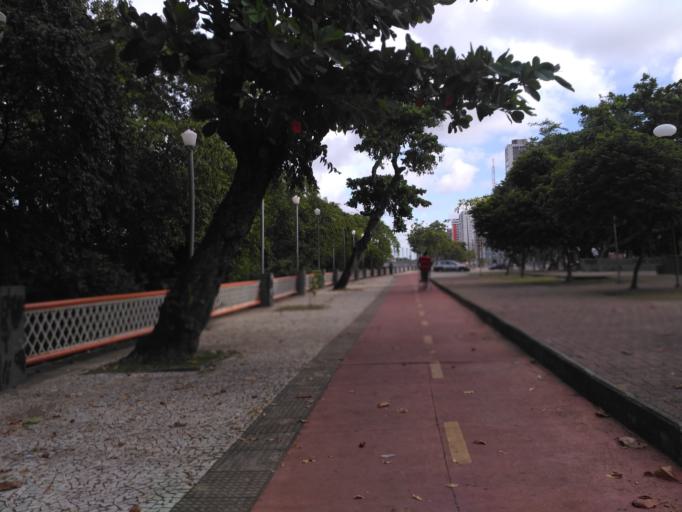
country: BR
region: Pernambuco
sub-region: Recife
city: Recife
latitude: -8.0569
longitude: -34.8779
